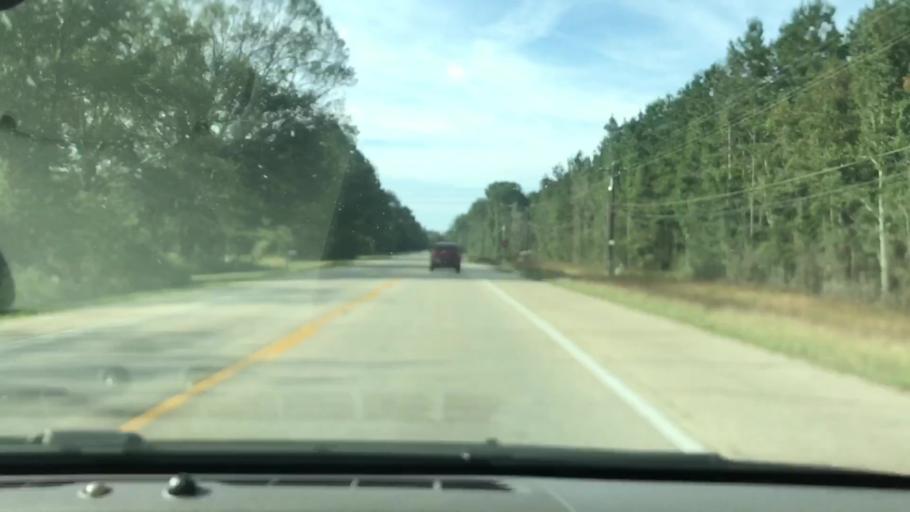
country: US
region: Louisiana
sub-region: Saint Tammany Parish
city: Pearl River
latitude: 30.4418
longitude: -89.7916
